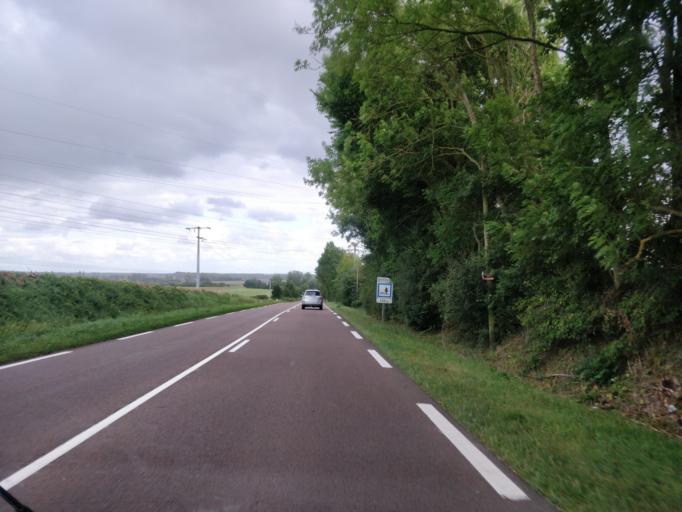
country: FR
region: Champagne-Ardenne
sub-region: Departement de l'Aube
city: Lusigny-sur-Barse
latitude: 48.2718
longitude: 4.2067
